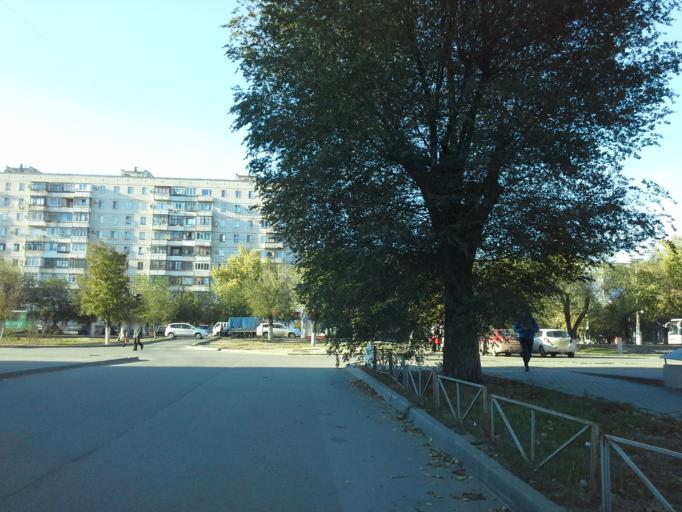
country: RU
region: Volgograd
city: Vodstroy
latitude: 48.8180
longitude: 44.6309
